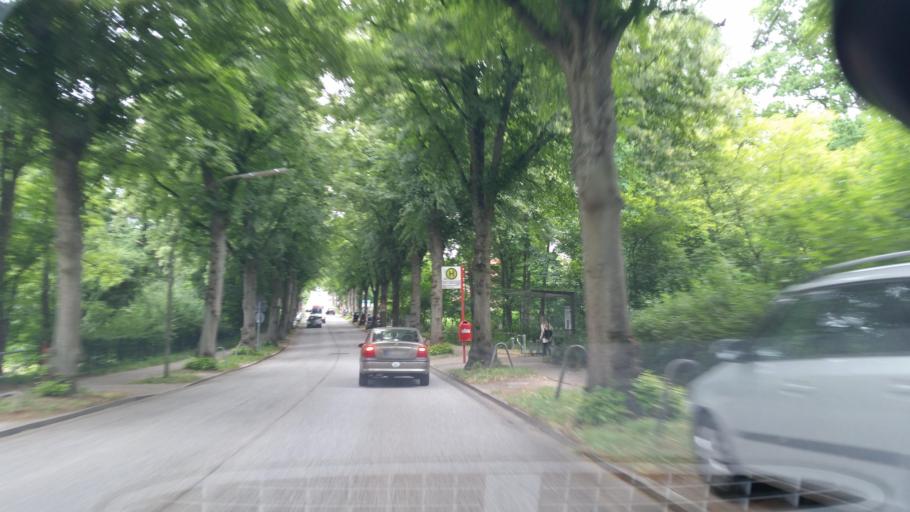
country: DE
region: Hamburg
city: Bergedorf
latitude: 53.4837
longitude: 10.2341
